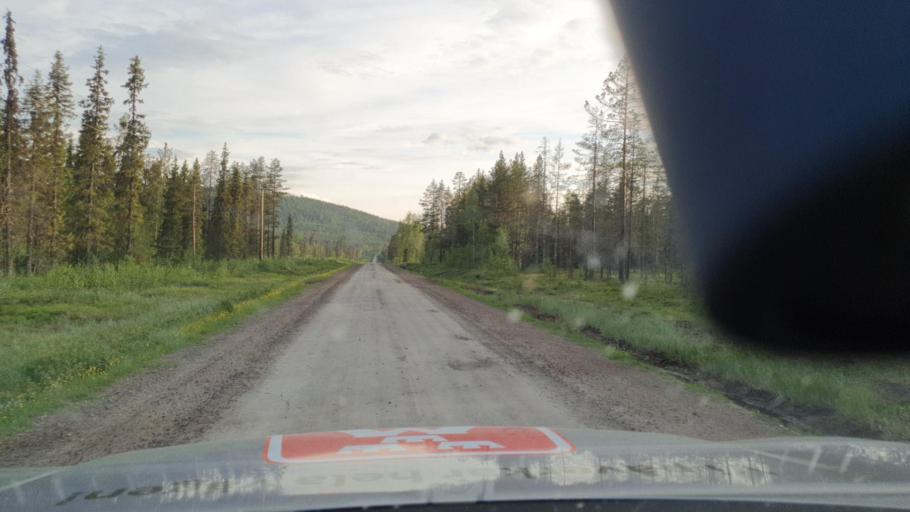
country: SE
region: Norrbotten
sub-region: Bodens Kommun
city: Boden
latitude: 66.4002
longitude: 21.6783
